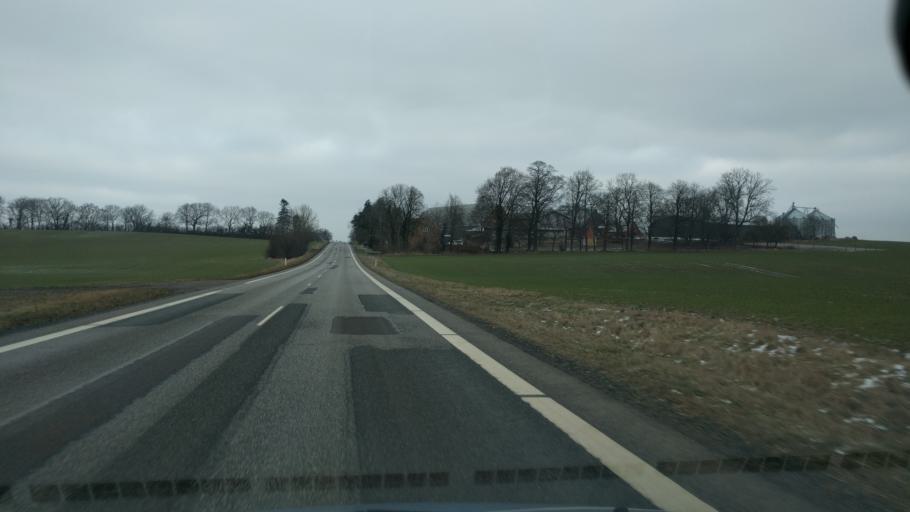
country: DK
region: Zealand
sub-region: Guldborgsund Kommune
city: Stubbekobing
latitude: 54.8441
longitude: 12.0073
